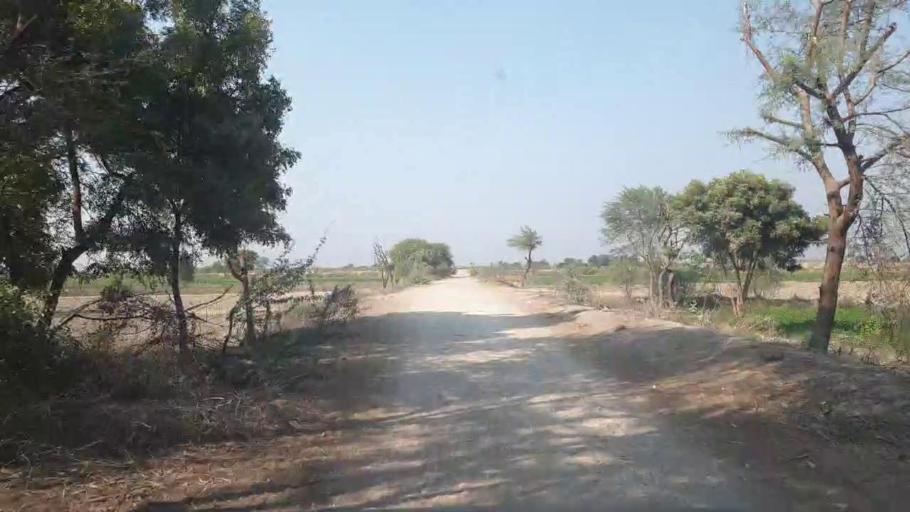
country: PK
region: Sindh
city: Tando Allahyar
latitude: 25.4424
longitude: 68.7875
